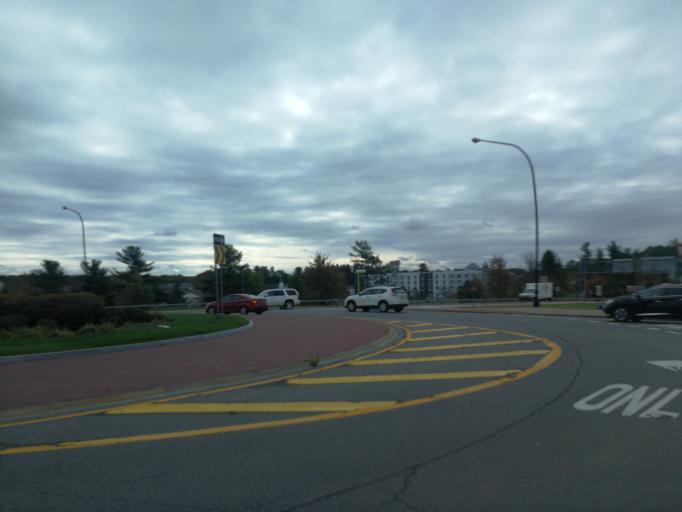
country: US
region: New York
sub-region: Saratoga County
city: Country Knolls
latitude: 42.9705
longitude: -73.8010
